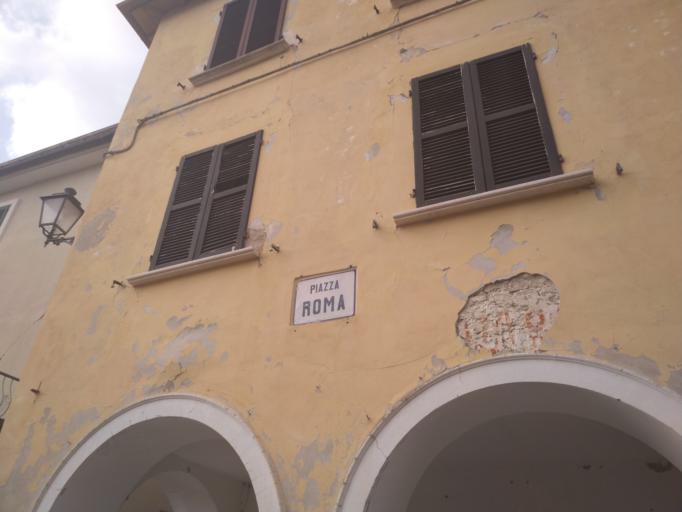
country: IT
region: Abruzzo
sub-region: Provincia di Teramo
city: Castelli
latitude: 42.4894
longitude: 13.7117
